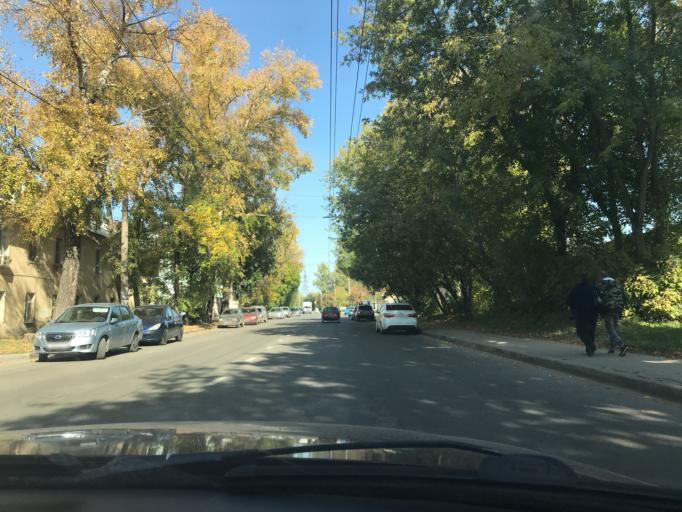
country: RU
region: Kaluga
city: Kaluga
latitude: 54.5403
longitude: 36.2794
